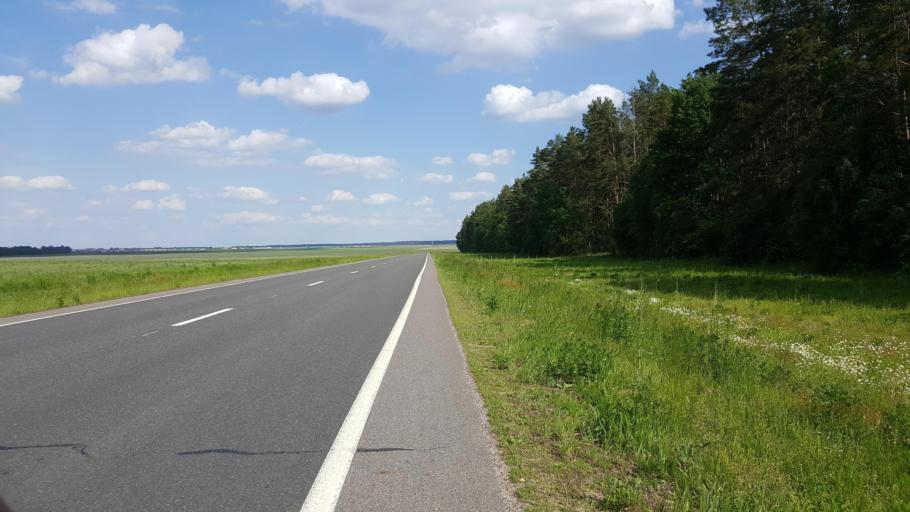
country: BY
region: Brest
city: Pruzhany
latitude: 52.5498
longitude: 24.1443
